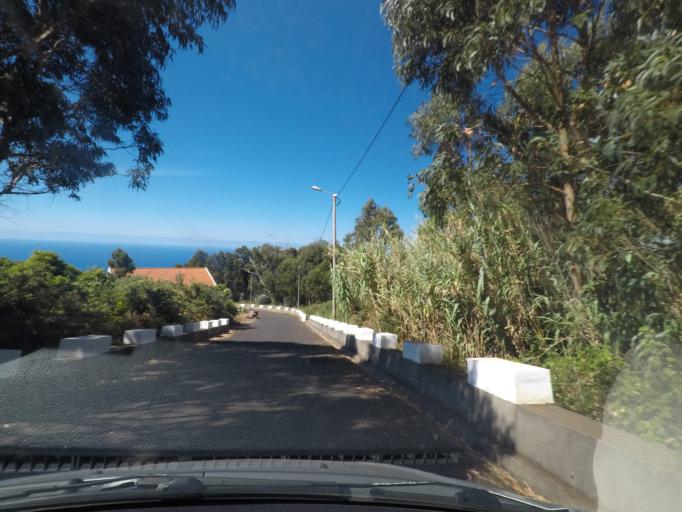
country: PT
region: Madeira
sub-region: Porto Moniz
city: Porto Moniz
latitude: 32.8588
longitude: -17.2012
